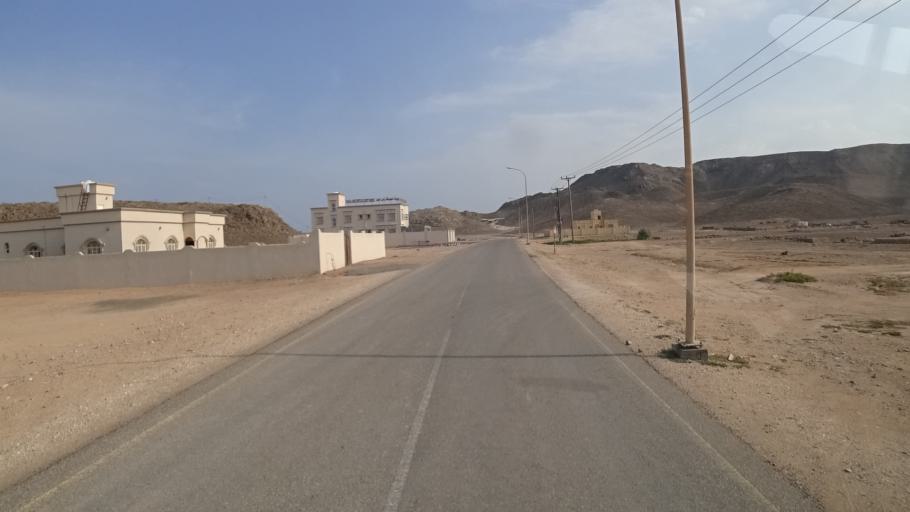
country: OM
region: Ash Sharqiyah
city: Sur
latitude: 22.4314
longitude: 59.8253
